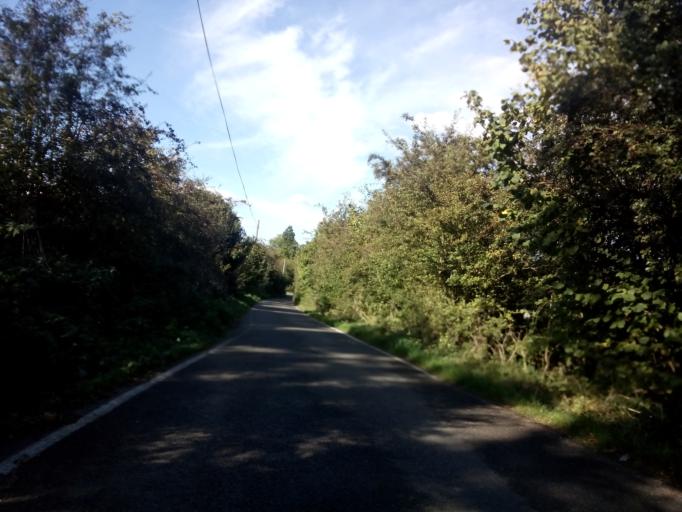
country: GB
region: England
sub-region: Suffolk
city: Ipswich
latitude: 52.0329
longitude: 1.1238
